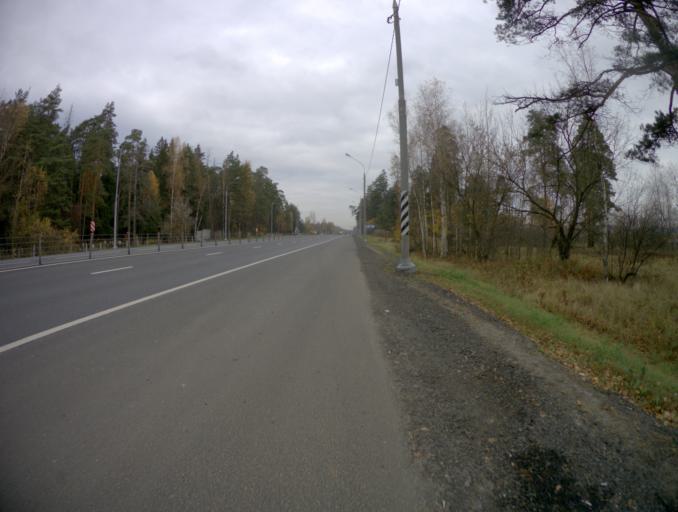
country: RU
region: Moskovskaya
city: Malaya Dubna
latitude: 55.8457
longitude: 38.9651
